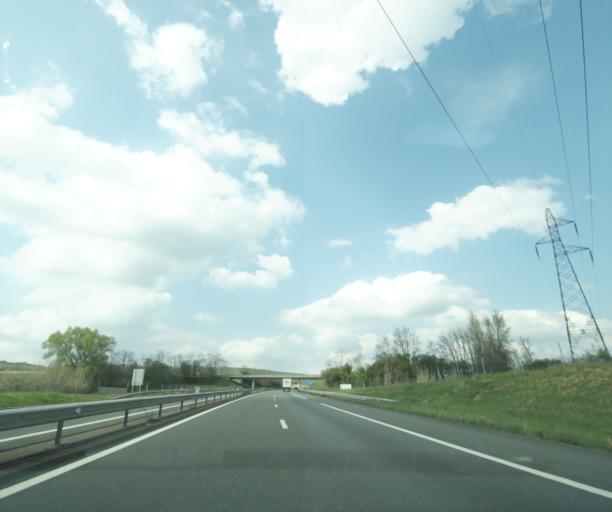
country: FR
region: Auvergne
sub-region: Departement du Puy-de-Dome
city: Saint-Bonnet-pres-Riom
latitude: 45.9559
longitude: 3.1046
